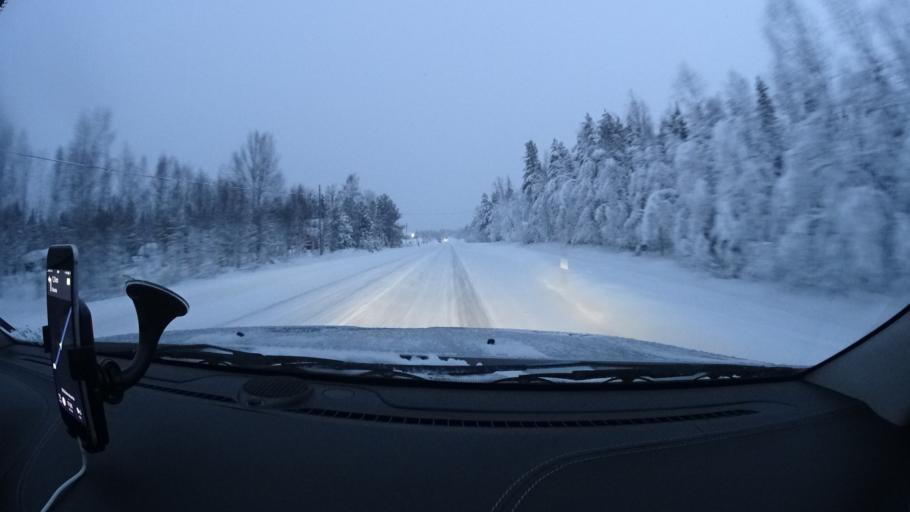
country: FI
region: Lapland
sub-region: Tunturi-Lappi
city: Kittilae
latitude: 67.6657
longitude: 24.8581
